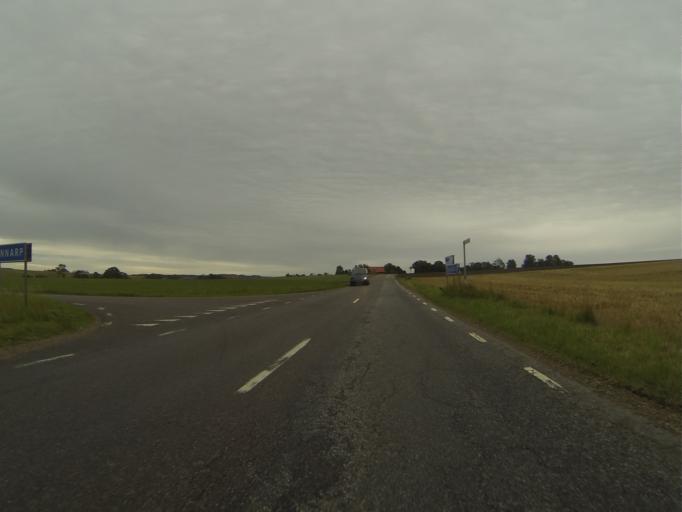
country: SE
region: Skane
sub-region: Lunds Kommun
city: Genarp
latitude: 55.6182
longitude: 13.3293
